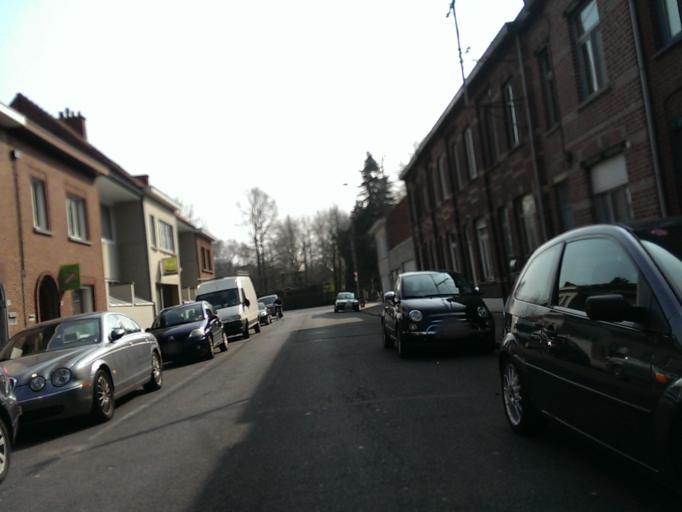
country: BE
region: Flanders
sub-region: Provincie West-Vlaanderen
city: Roeselare
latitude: 50.9468
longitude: 3.1395
